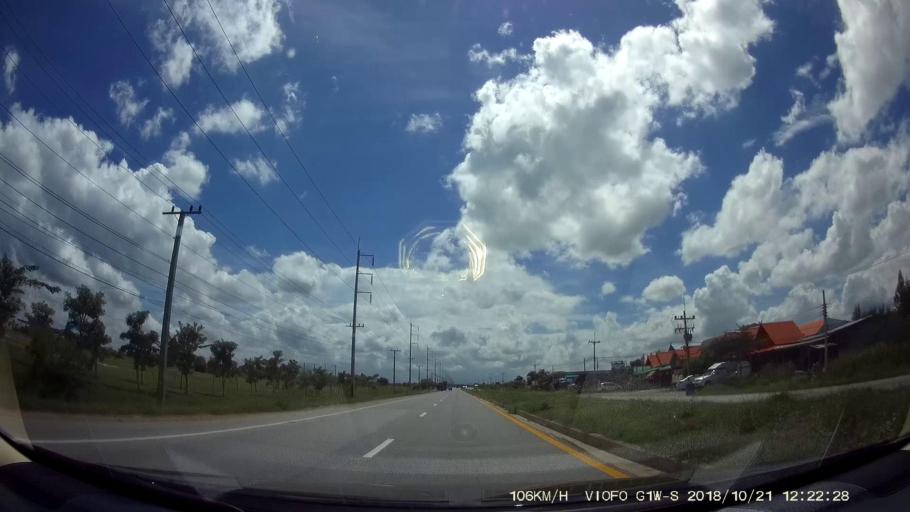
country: TH
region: Nakhon Ratchasima
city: Dan Khun Thot
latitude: 15.2607
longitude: 101.7896
